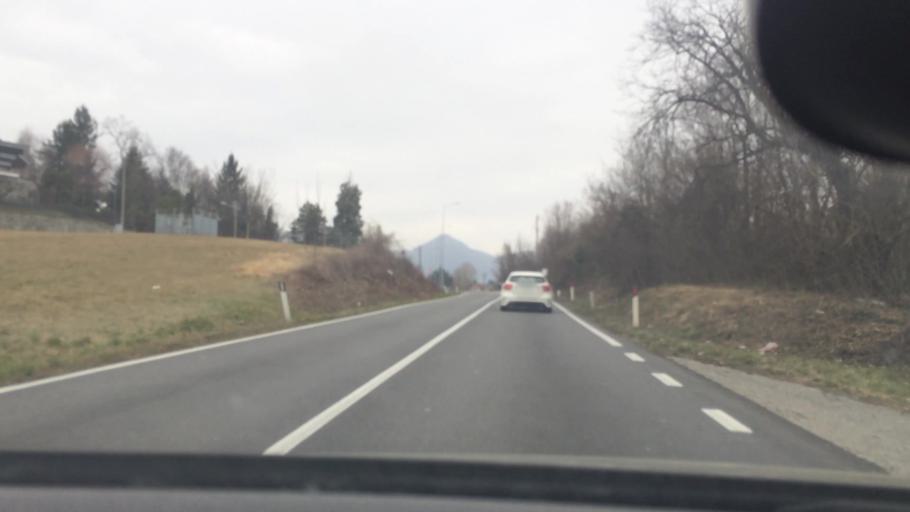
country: IT
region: Lombardy
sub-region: Provincia di Como
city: Nobile-Monguzzo
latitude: 45.7703
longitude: 9.2299
